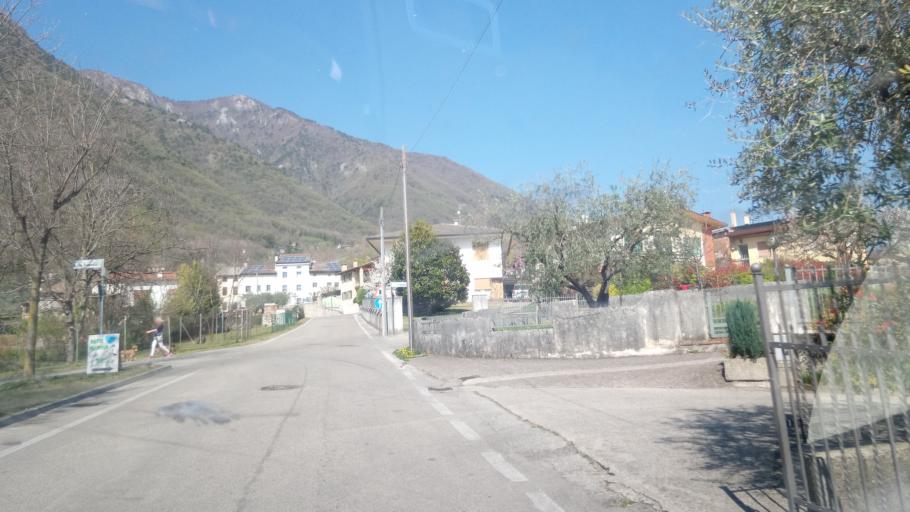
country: IT
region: Veneto
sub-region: Provincia di Treviso
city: Borso del Grappa
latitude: 45.8106
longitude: 11.7729
